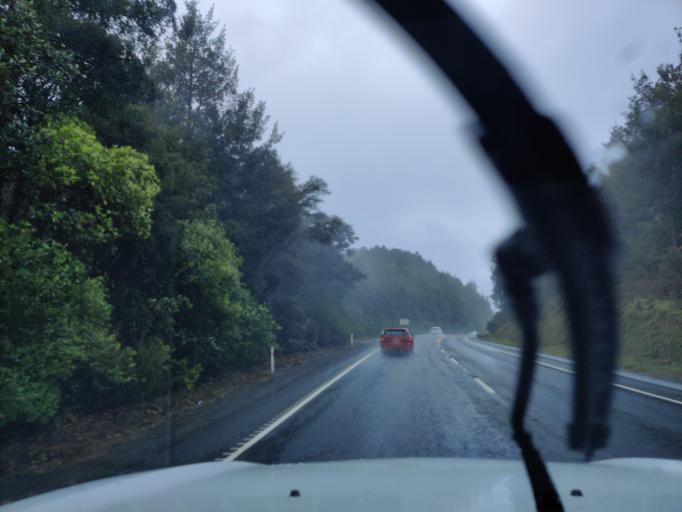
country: NZ
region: Waikato
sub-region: South Waikato District
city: Tokoroa
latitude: -38.0088
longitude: 175.9307
